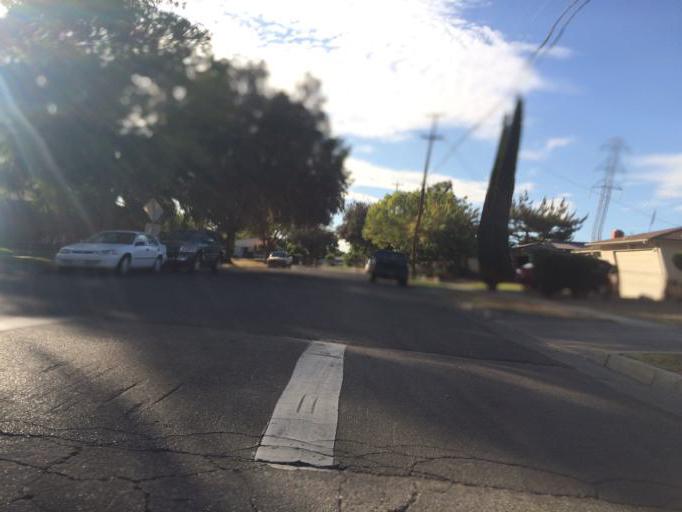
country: US
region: California
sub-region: Fresno County
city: Sunnyside
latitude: 36.7604
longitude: -119.7301
